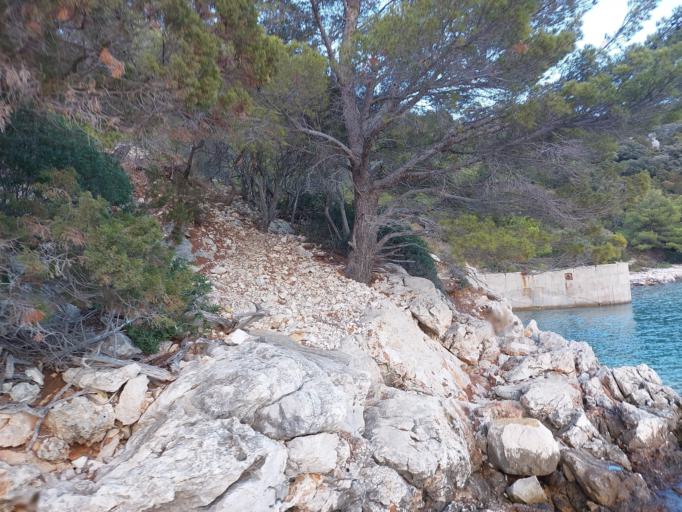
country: HR
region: Dubrovacko-Neretvanska
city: Smokvica
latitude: 42.7676
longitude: 16.8021
